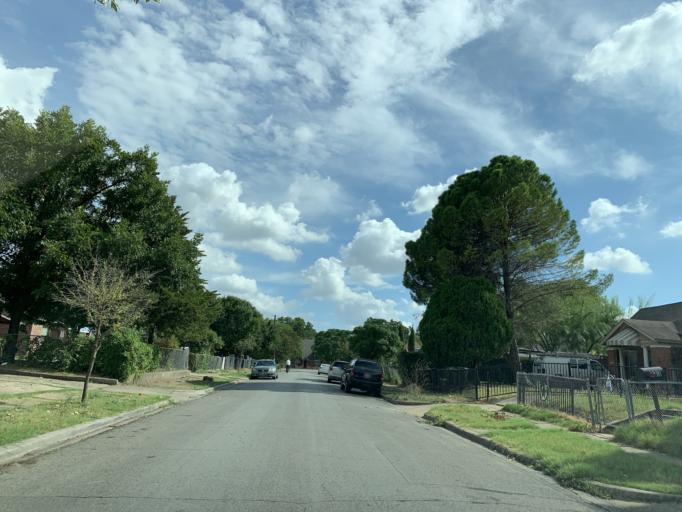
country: US
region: Texas
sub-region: Dallas County
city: Cockrell Hill
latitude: 32.7364
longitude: -96.8480
